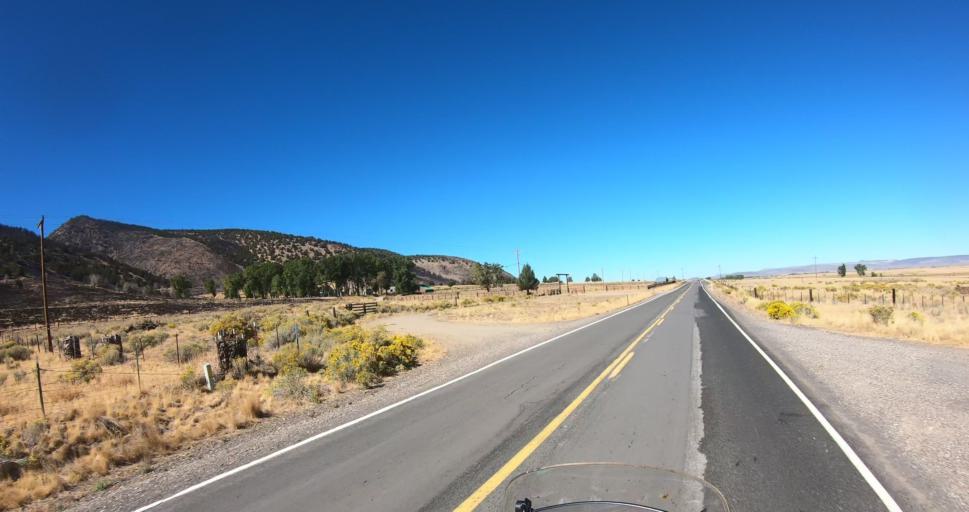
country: US
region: Oregon
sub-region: Lake County
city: Lakeview
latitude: 42.6417
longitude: -120.5199
